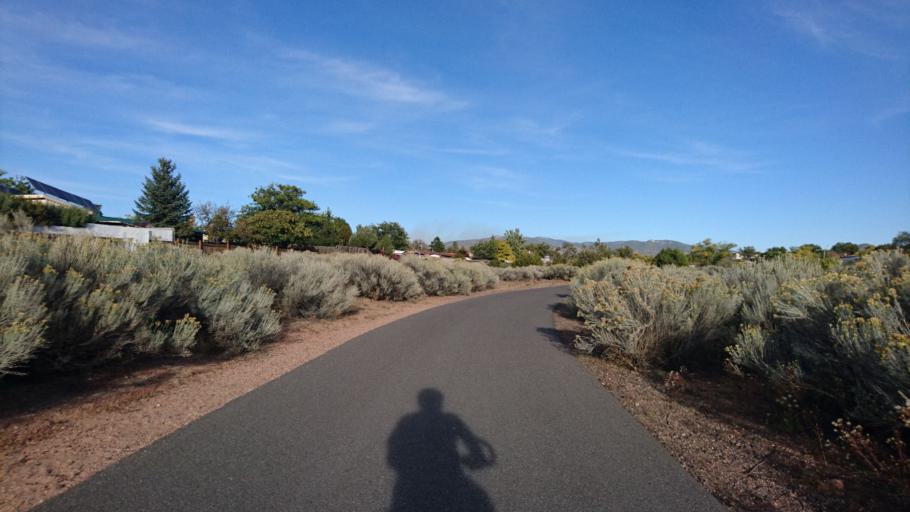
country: US
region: New Mexico
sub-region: Santa Fe County
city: Agua Fria
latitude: 35.6422
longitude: -105.9863
